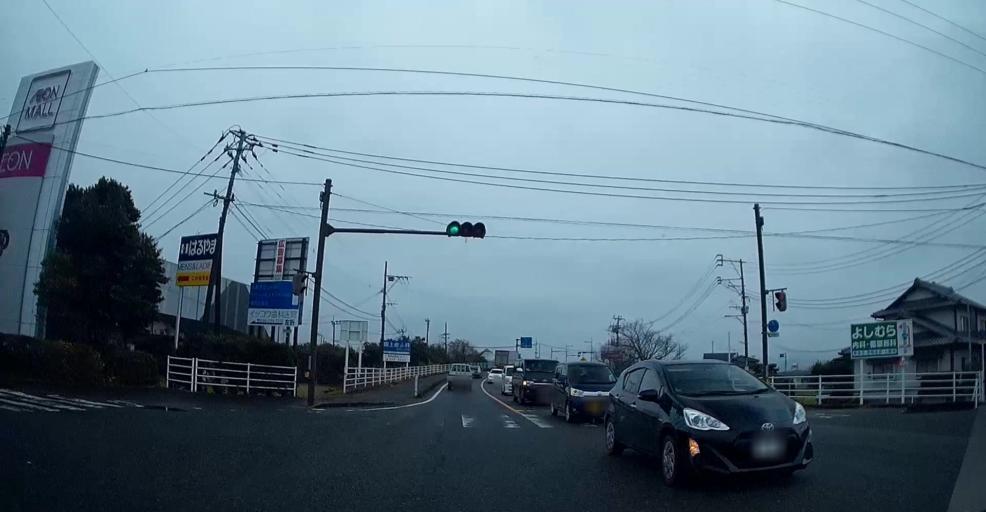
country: JP
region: Kumamoto
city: Kumamoto
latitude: 32.7398
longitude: 130.7404
